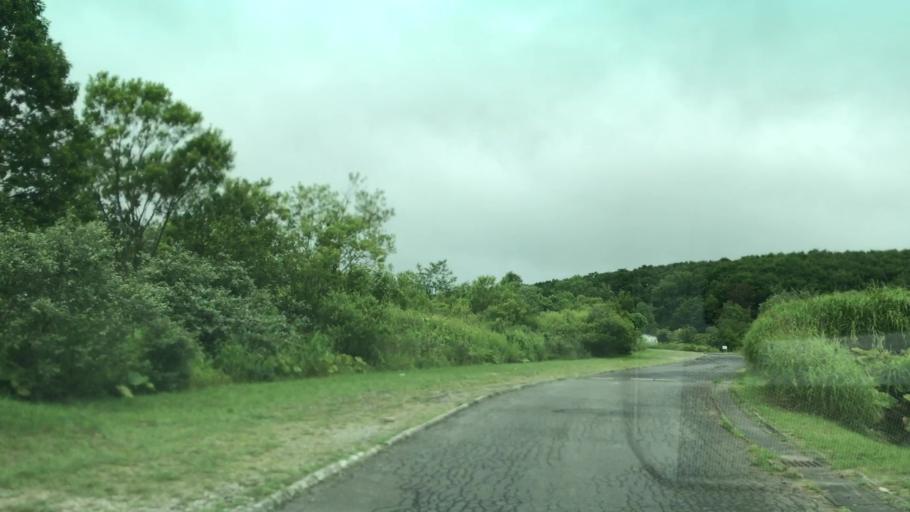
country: JP
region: Hokkaido
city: Muroran
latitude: 42.3944
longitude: 141.0001
